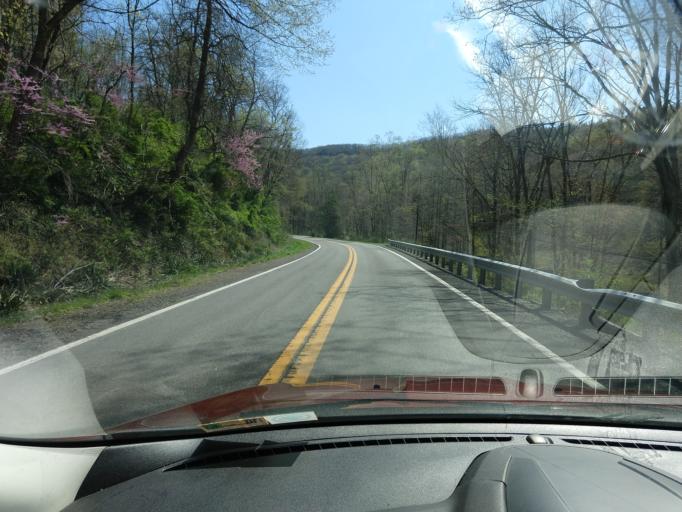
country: US
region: West Virginia
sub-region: Greenbrier County
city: Alderson
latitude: 37.7170
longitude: -80.6193
